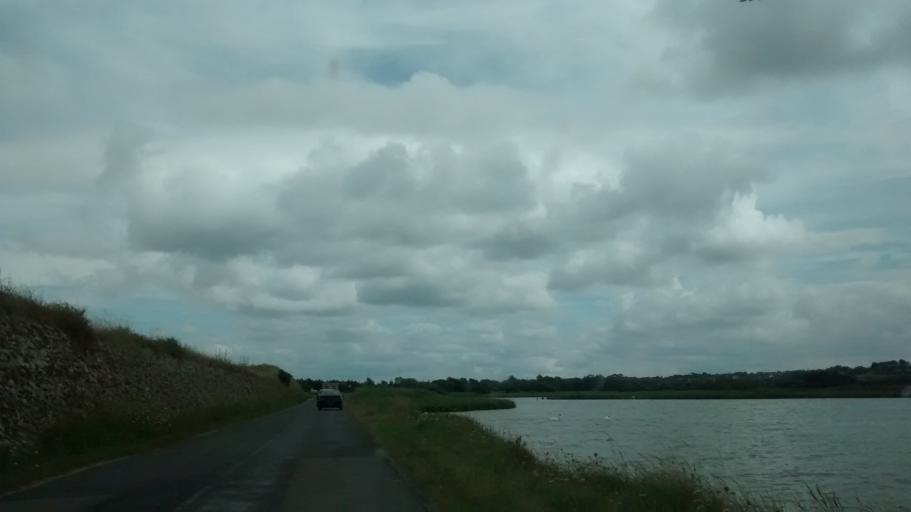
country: FR
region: Brittany
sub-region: Departement du Finistere
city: Guisseny
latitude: 48.6359
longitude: -4.4362
